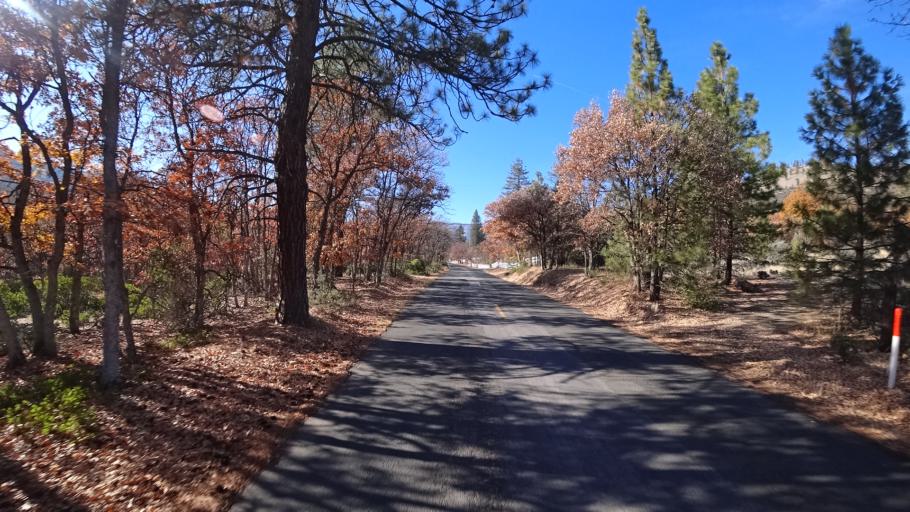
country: US
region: California
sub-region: Siskiyou County
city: Yreka
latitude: 41.7165
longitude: -122.6638
